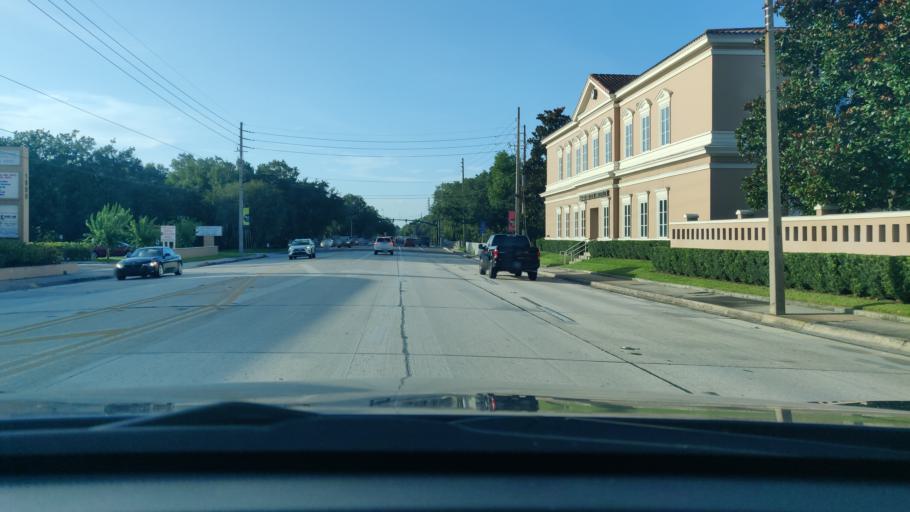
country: US
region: Florida
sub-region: Orange County
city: Orlando
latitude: 28.5688
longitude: -81.3644
